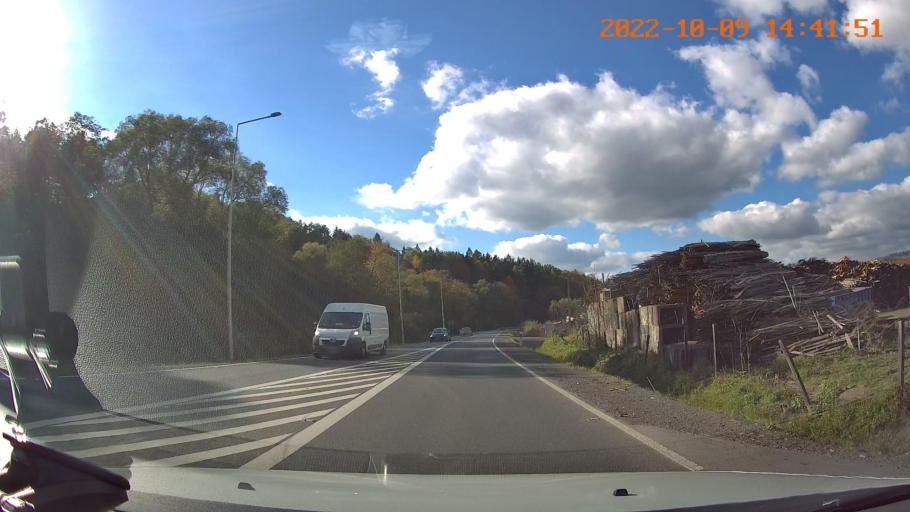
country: PL
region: Lesser Poland Voivodeship
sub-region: Powiat myslenicki
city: Lubien
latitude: 49.7105
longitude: 20.0076
